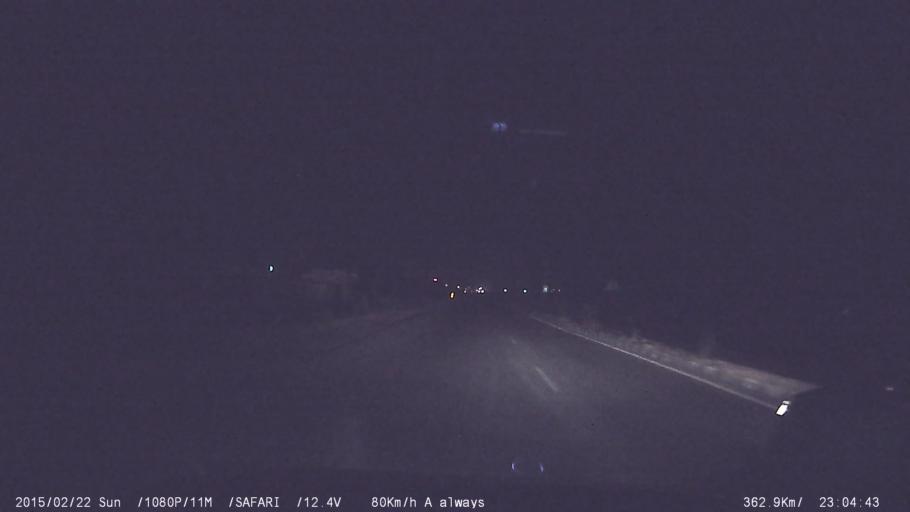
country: IN
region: Tamil Nadu
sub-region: Namakkal
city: Rasipuram
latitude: 11.4059
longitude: 78.1593
